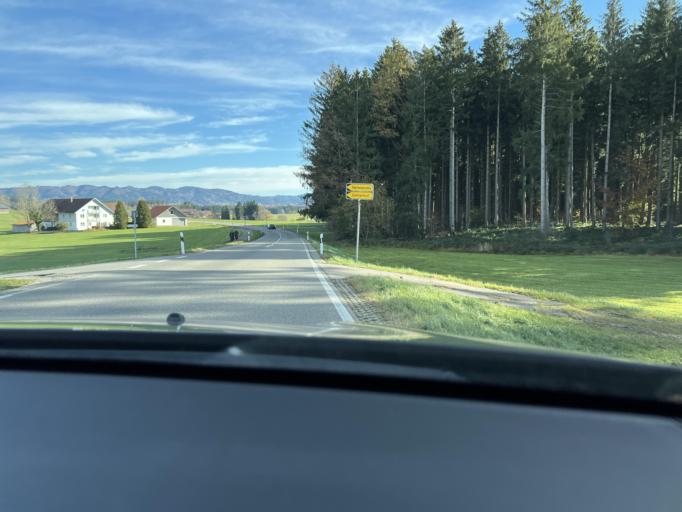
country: DE
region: Bavaria
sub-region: Swabia
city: Gestratz
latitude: 47.7050
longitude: 9.9809
